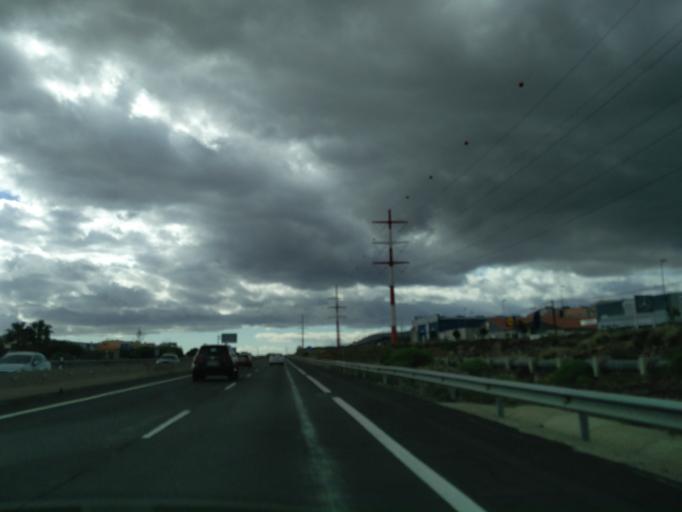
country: ES
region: Canary Islands
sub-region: Provincia de Santa Cruz de Tenerife
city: San Miguel
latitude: 28.0510
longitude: -16.6190
